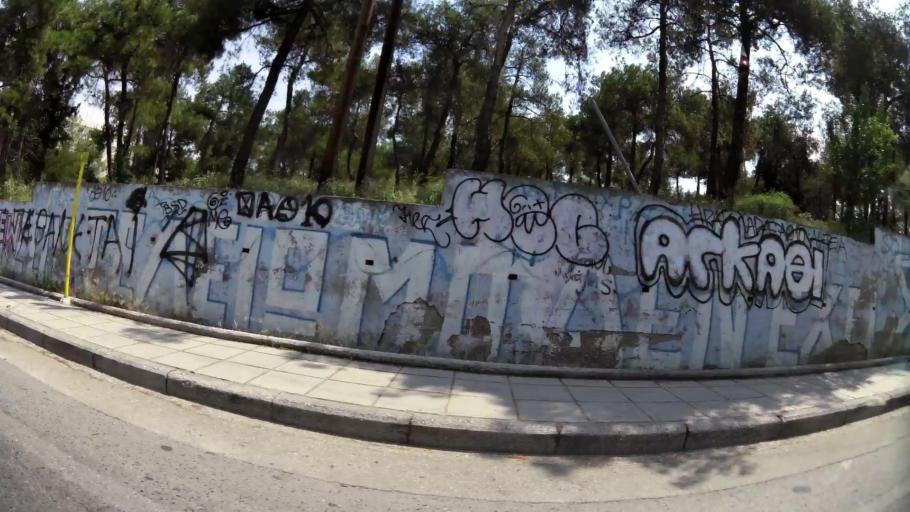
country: GR
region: Central Macedonia
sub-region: Nomos Thessalonikis
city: Agios Pavlos
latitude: 40.6289
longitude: 22.9687
